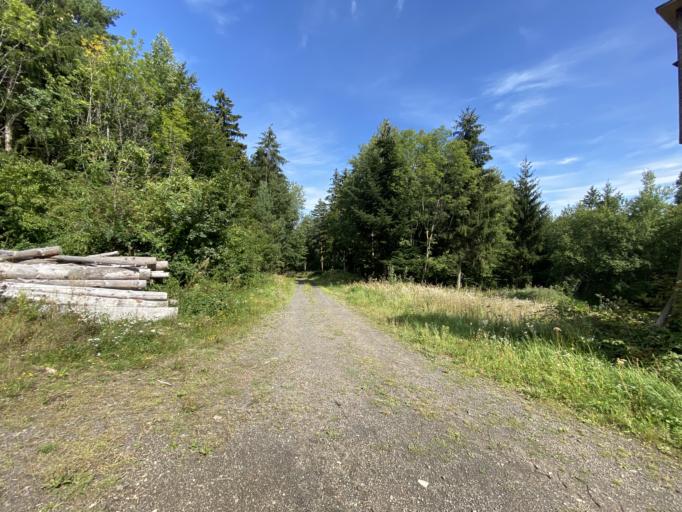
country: AT
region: Burgenland
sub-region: Politischer Bezirk Oberpullendorf
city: Kobersdorf
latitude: 47.5723
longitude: 16.3576
